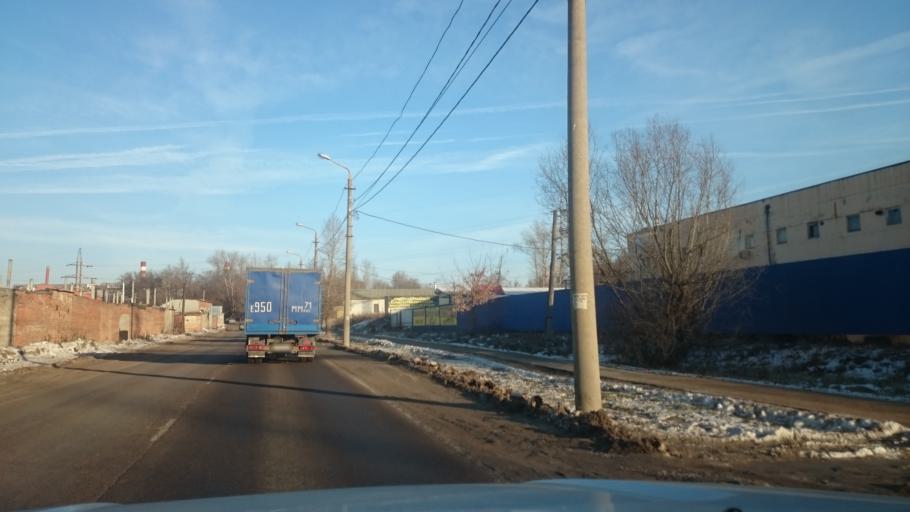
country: RU
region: Tula
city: Tula
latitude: 54.2174
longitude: 37.6855
